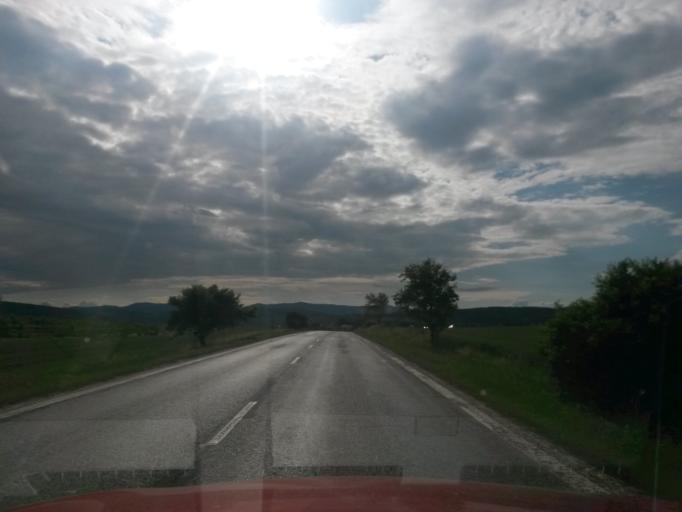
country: SK
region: Presovsky
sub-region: Okres Presov
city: Presov
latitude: 49.0086
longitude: 21.1374
